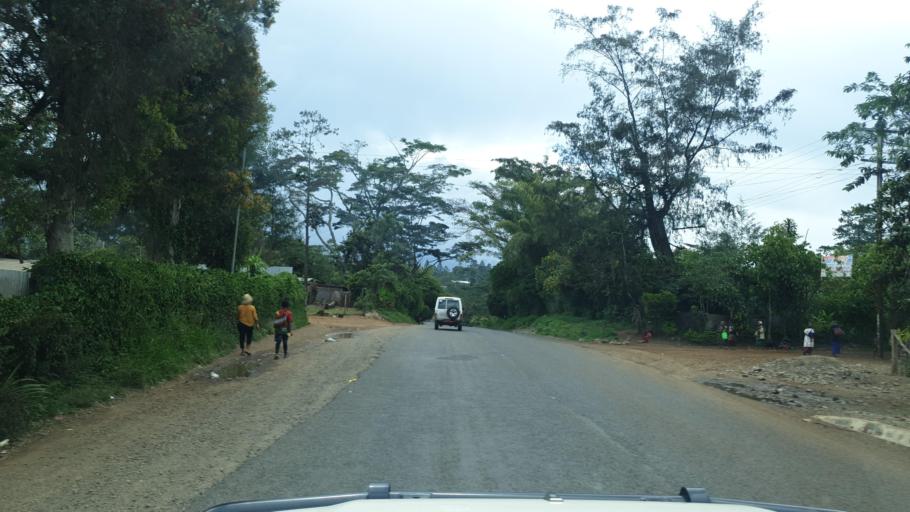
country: PG
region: Eastern Highlands
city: Goroka
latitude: -6.0471
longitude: 145.3788
